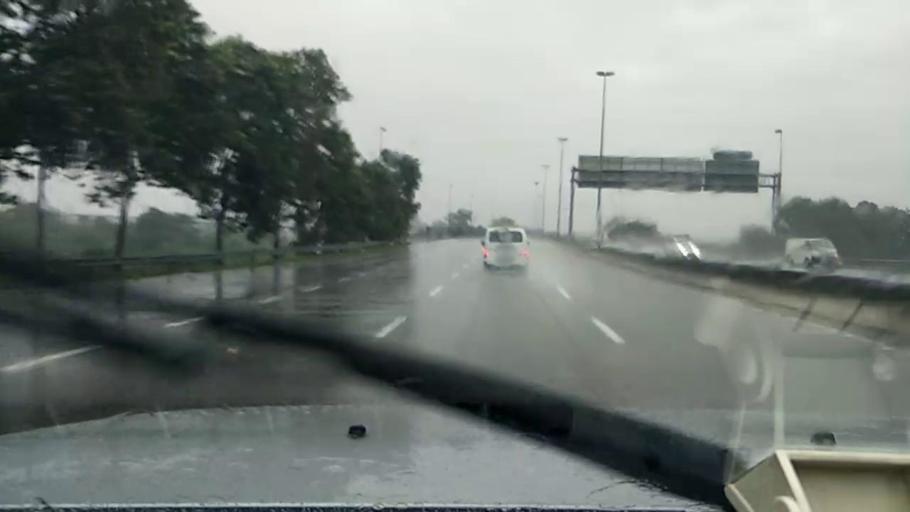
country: MY
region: Selangor
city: Kampong Baharu Balakong
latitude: 2.9946
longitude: 101.7743
